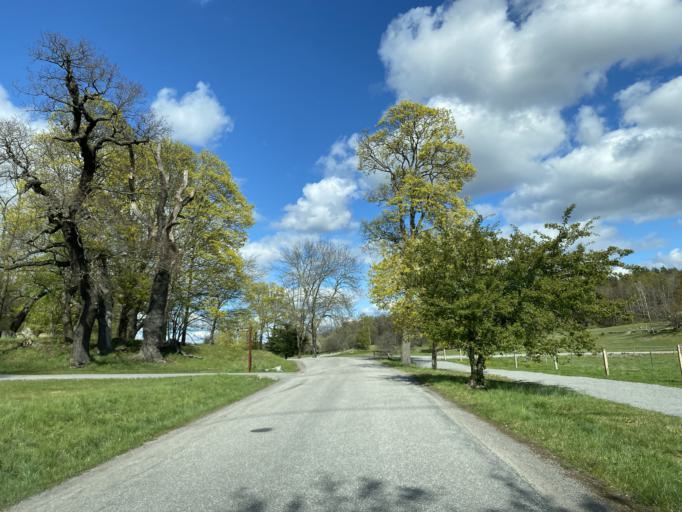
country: SE
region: Stockholm
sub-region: Stockholms Kommun
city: OEstermalm
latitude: 59.3637
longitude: 18.0845
